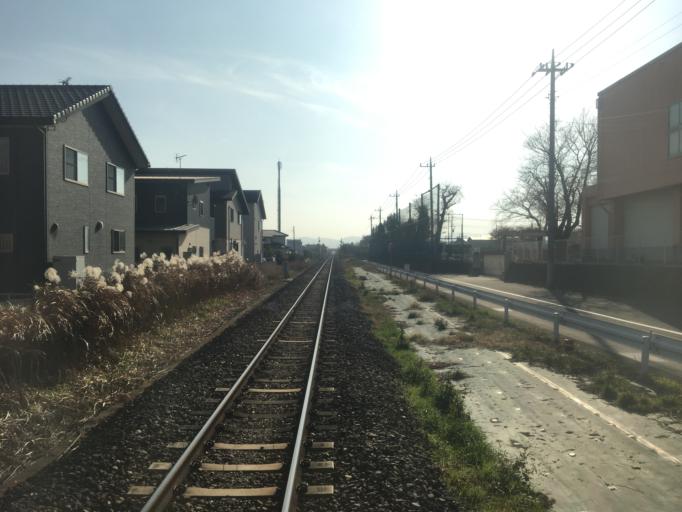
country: JP
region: Gunma
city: Fujioka
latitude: 36.2588
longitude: 139.0835
